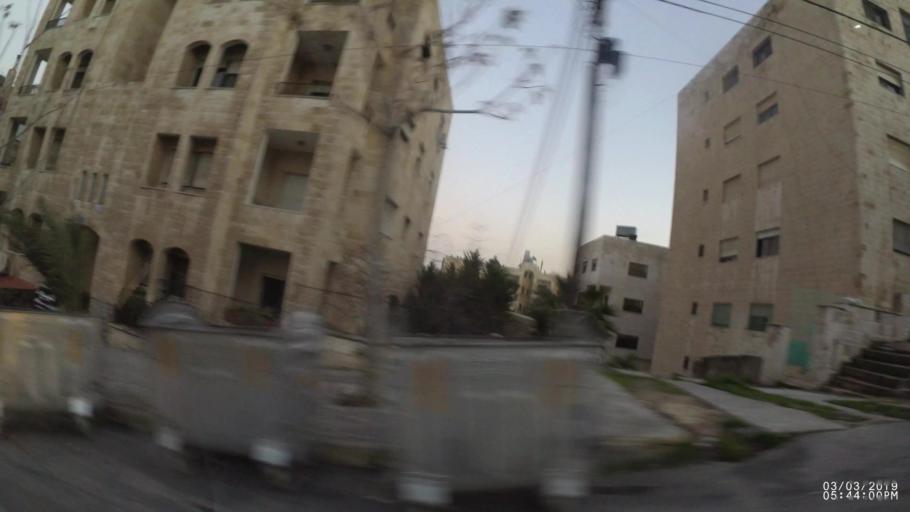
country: JO
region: Amman
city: Al Jubayhah
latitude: 31.9871
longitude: 35.8916
